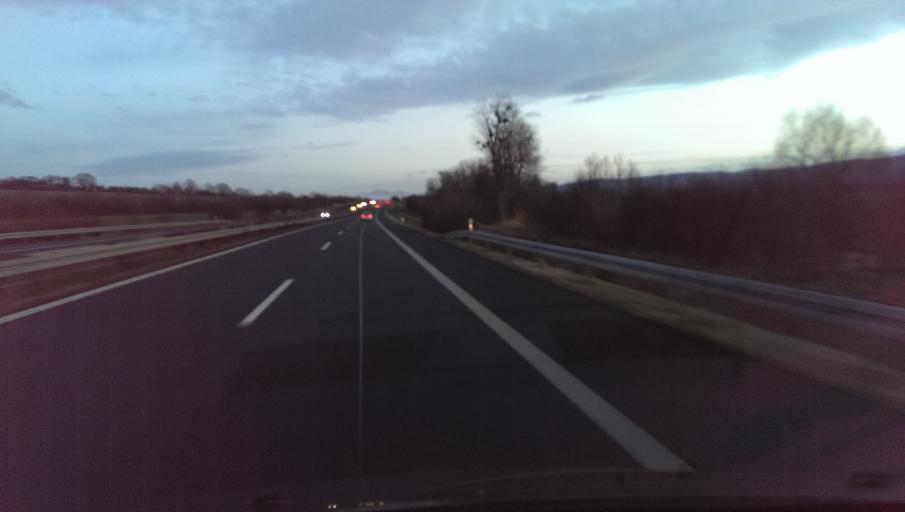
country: DE
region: Saxony-Anhalt
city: Stapelburg
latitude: 51.9260
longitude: 10.6529
